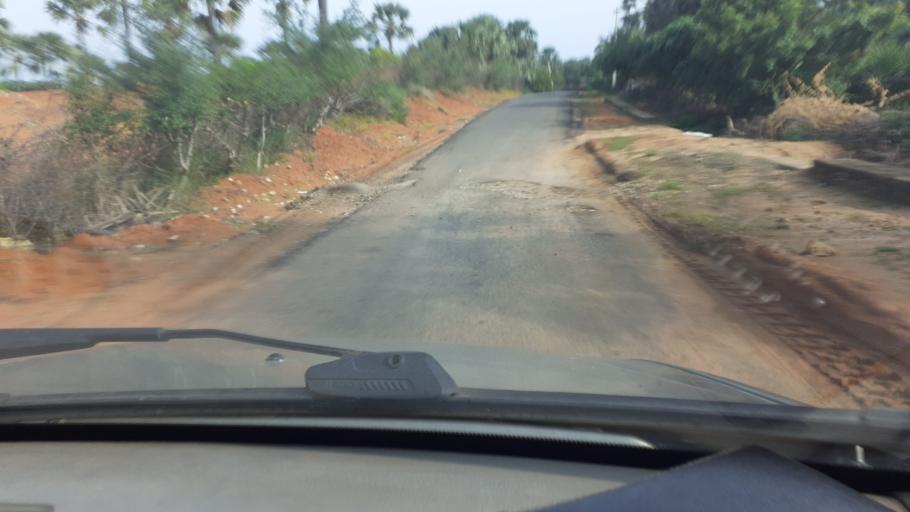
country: IN
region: Tamil Nadu
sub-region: Tirunelveli Kattabo
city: Tisaiyanvilai
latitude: 8.3372
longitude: 77.9478
